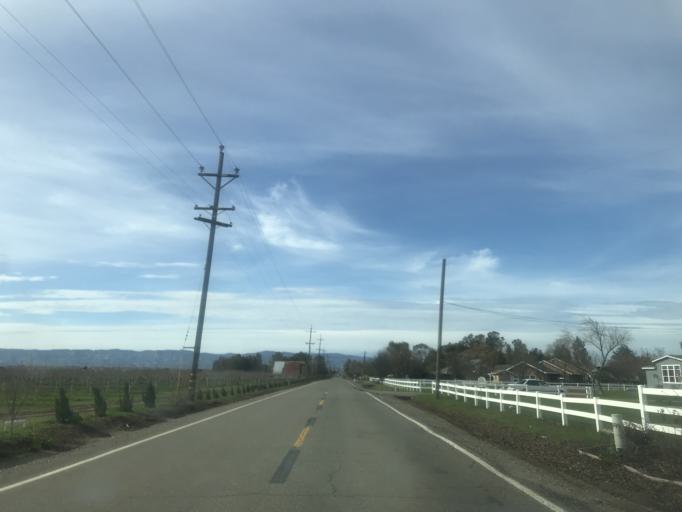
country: US
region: California
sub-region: Yolo County
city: Cottonwood
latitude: 38.6635
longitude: -121.8816
